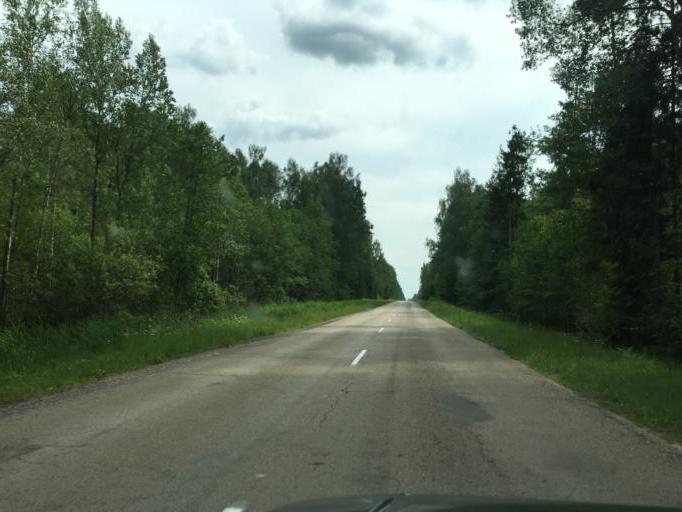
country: LV
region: Rugaju
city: Rugaji
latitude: 56.7804
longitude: 27.1043
